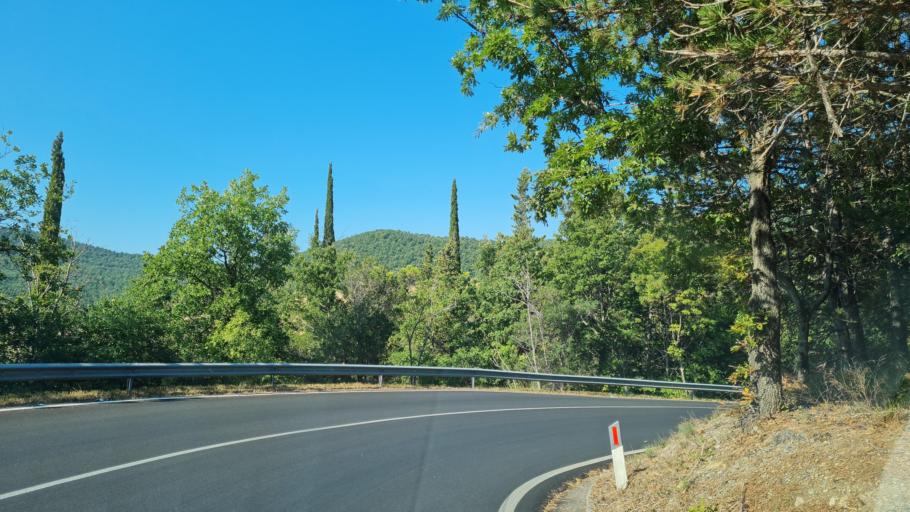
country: IT
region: Tuscany
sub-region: Provincia di Siena
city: Chianciano Terme
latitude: 43.0340
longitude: 11.7988
